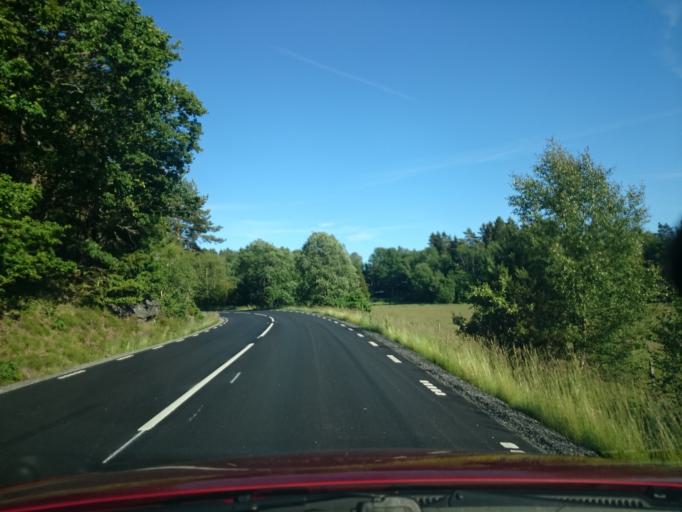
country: SE
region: Vaestra Goetaland
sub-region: Lerums Kommun
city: Lerum
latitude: 57.7901
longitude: 12.2283
